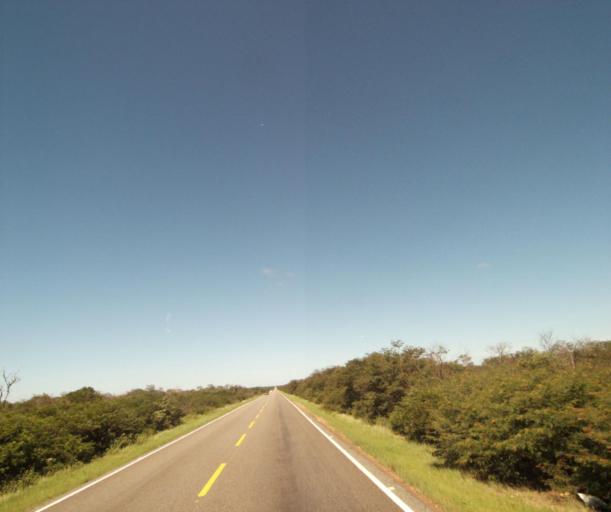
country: BR
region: Bahia
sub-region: Palmas De Monte Alto
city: Palmas de Monte Alto
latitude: -14.2516
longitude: -43.1885
